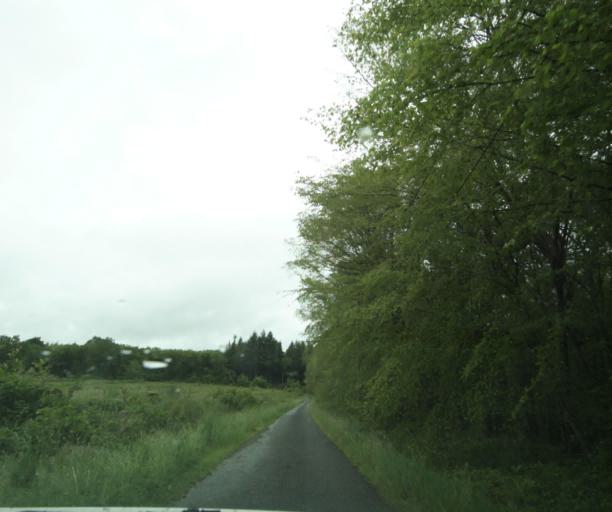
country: FR
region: Bourgogne
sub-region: Departement de Saone-et-Loire
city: Genelard
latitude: 46.5484
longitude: 4.2715
